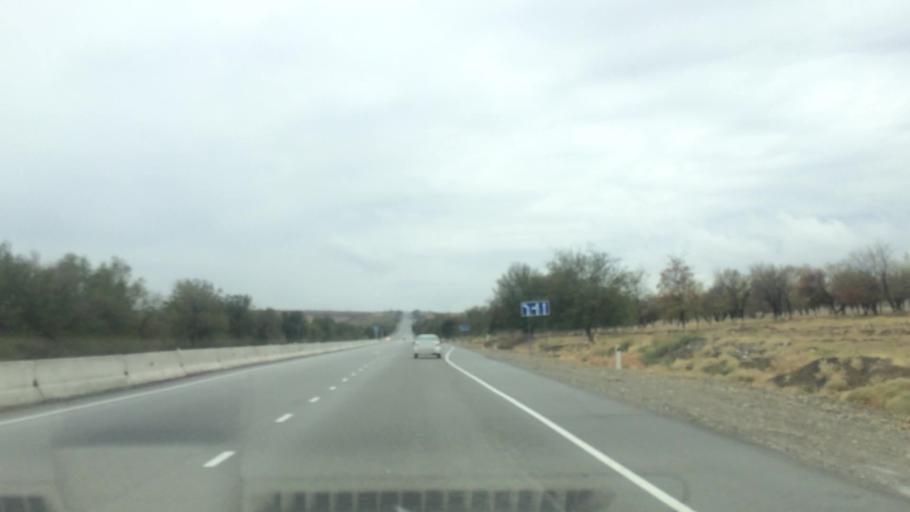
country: UZ
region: Samarqand
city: Bulung'ur
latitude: 39.8782
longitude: 67.4837
